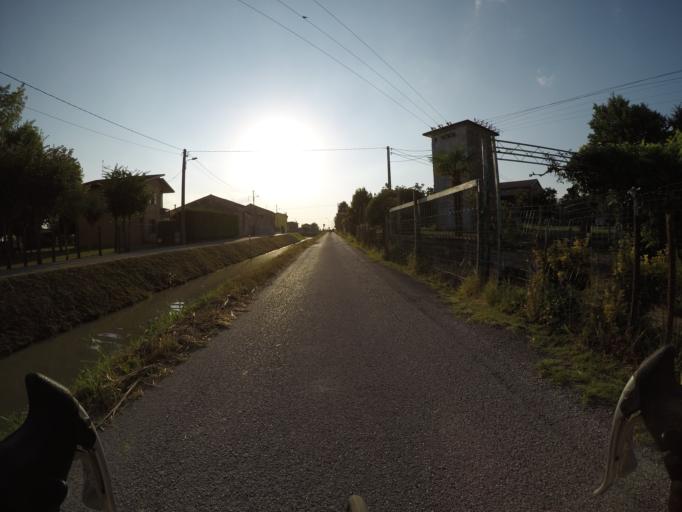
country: IT
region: Veneto
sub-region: Provincia di Rovigo
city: San Bellino
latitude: 45.0456
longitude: 11.5848
